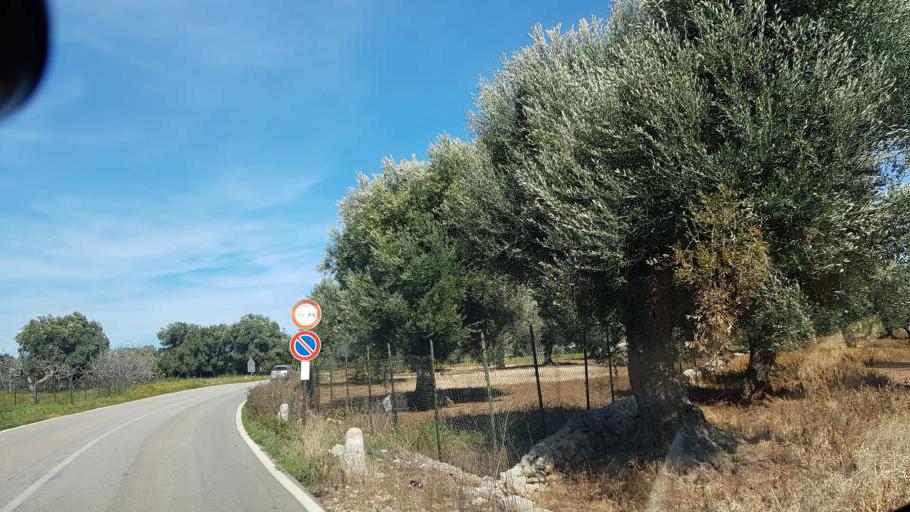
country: IT
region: Apulia
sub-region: Provincia di Brindisi
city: Pezze di Greco
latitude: 40.8367
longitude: 17.4608
